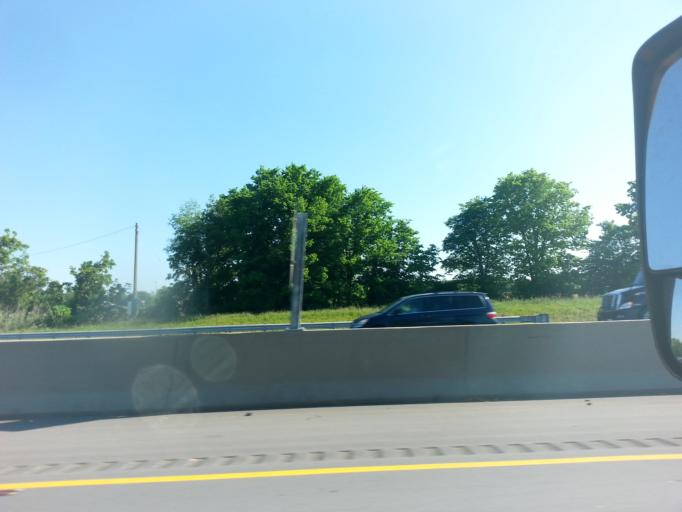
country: US
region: Kentucky
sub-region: Shelby County
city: Shelbyville
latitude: 38.1905
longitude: -85.2655
